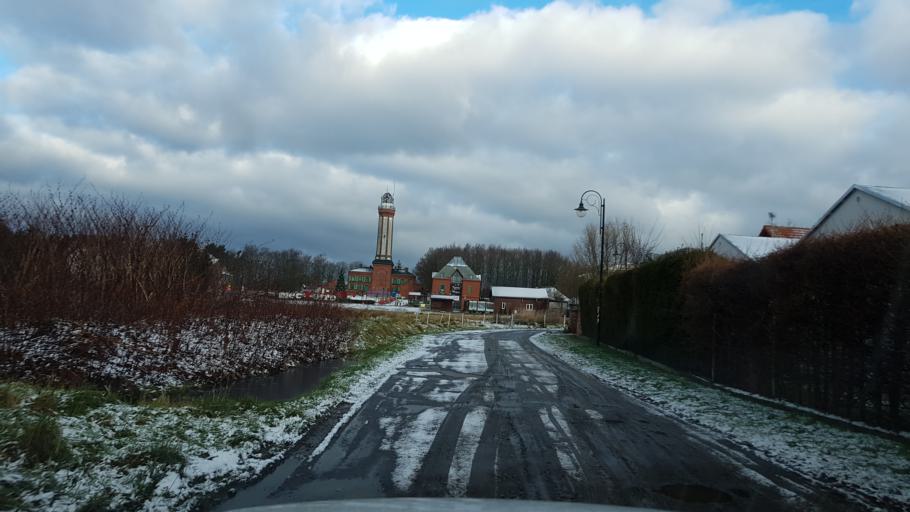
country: PL
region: West Pomeranian Voivodeship
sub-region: Powiat gryficki
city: Rewal
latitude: 54.0920
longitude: 15.0656
